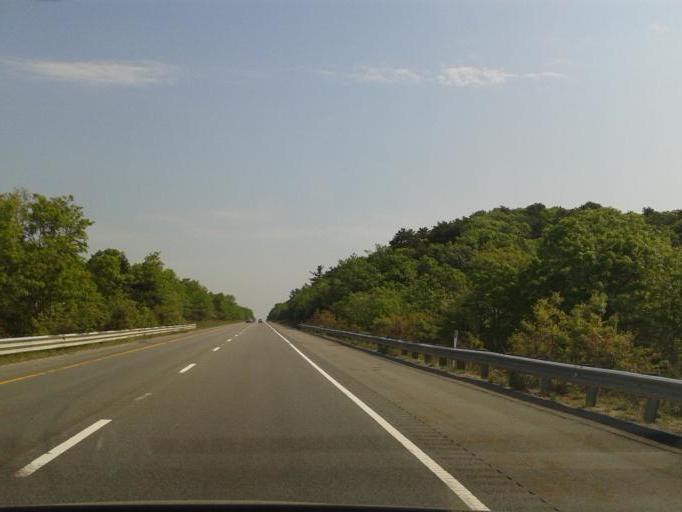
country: US
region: Massachusetts
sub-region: Barnstable County
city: North Falmouth
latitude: 41.6306
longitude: -70.6118
